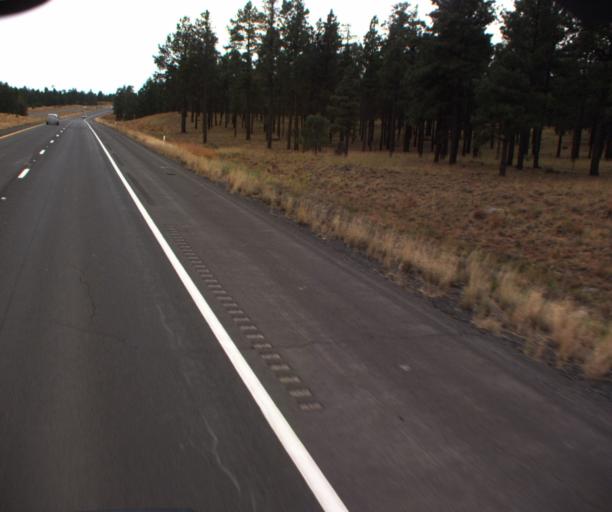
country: US
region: Arizona
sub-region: Coconino County
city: Flagstaff
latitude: 35.3688
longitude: -111.5742
